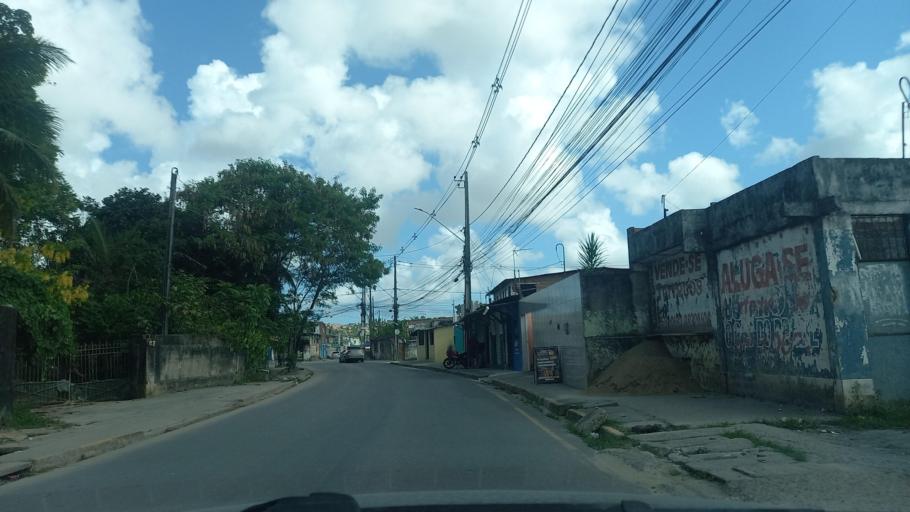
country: BR
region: Pernambuco
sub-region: Jaboatao Dos Guararapes
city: Jaboatao dos Guararapes
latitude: -8.1110
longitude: -34.9740
